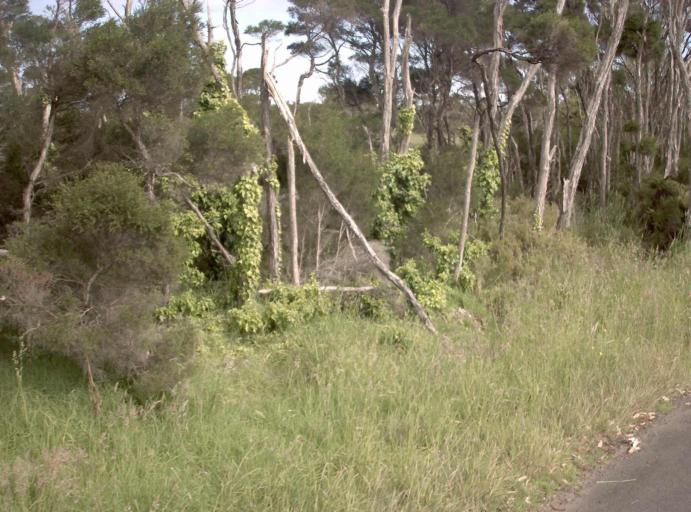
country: AU
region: Victoria
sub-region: Bass Coast
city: Phillip Island
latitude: -38.4767
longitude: 145.2390
